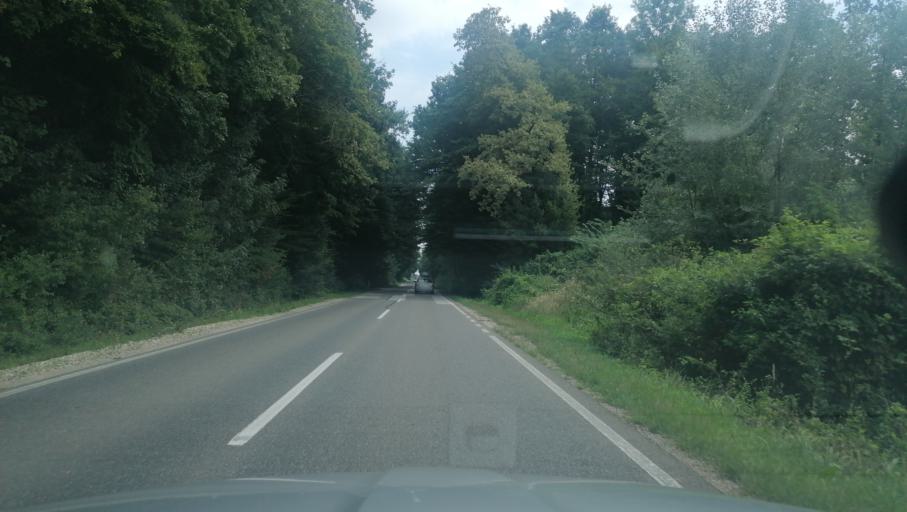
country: BA
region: Republika Srpska
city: Obudovac
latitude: 44.9493
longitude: 18.6546
